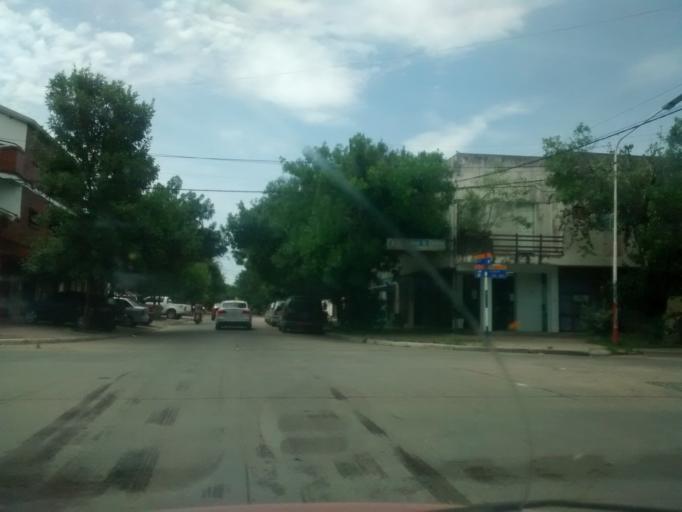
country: AR
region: Chaco
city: Resistencia
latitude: -27.4566
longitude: -58.9927
